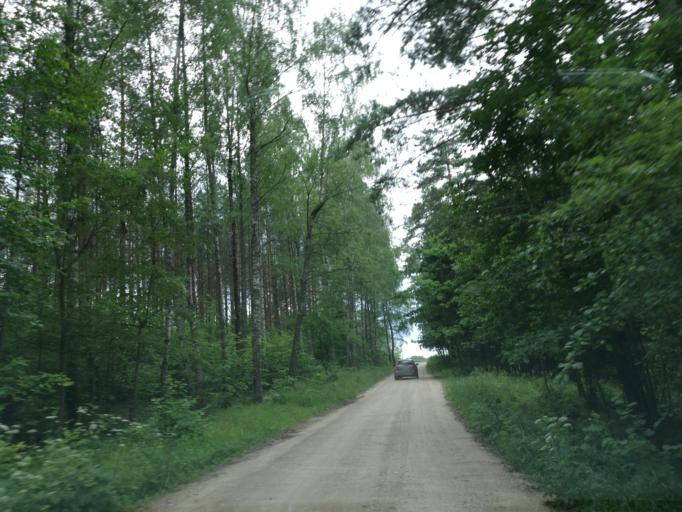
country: LT
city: Trakai
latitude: 54.6486
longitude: 24.9618
